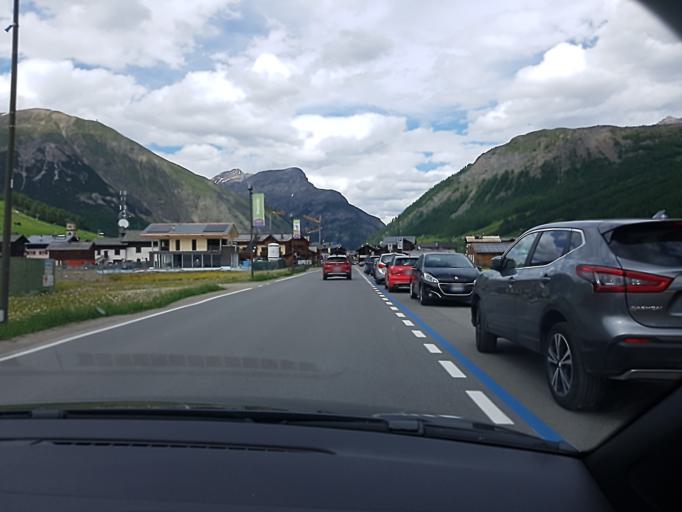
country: IT
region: Lombardy
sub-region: Provincia di Sondrio
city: Livigno
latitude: 46.5357
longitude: 10.1362
